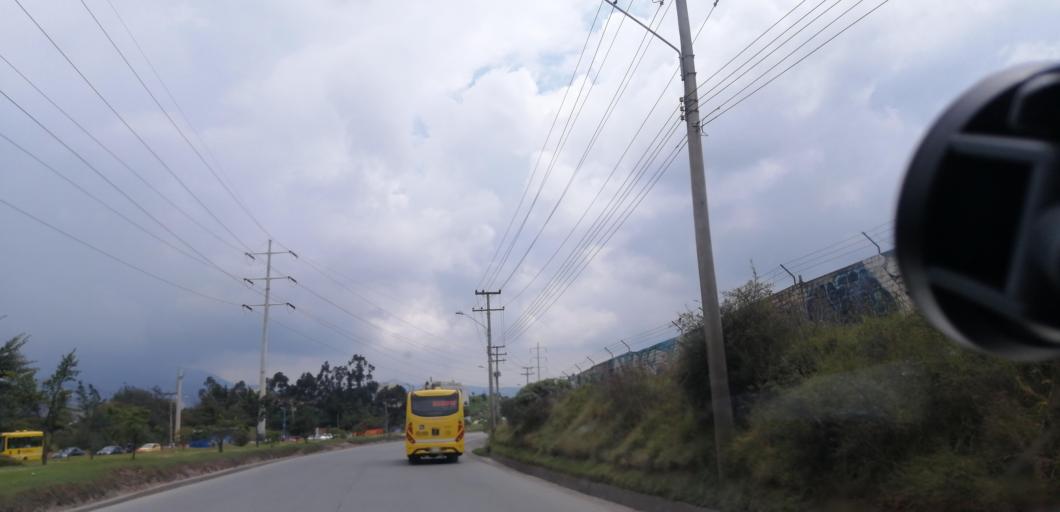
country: CO
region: Bogota D.C.
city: Bogota
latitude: 4.5354
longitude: -74.1283
